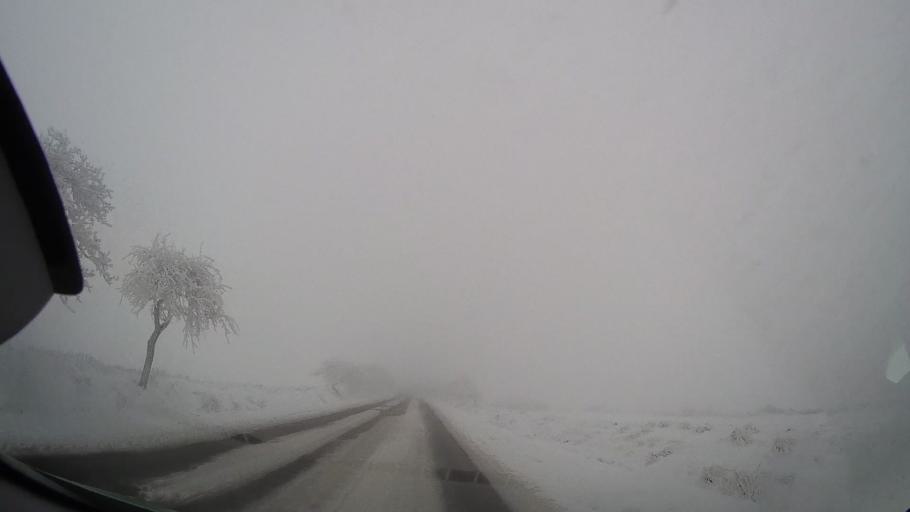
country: RO
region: Neamt
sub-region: Comuna Valea Ursului
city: Valea Ursului
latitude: 46.8214
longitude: 27.0637
